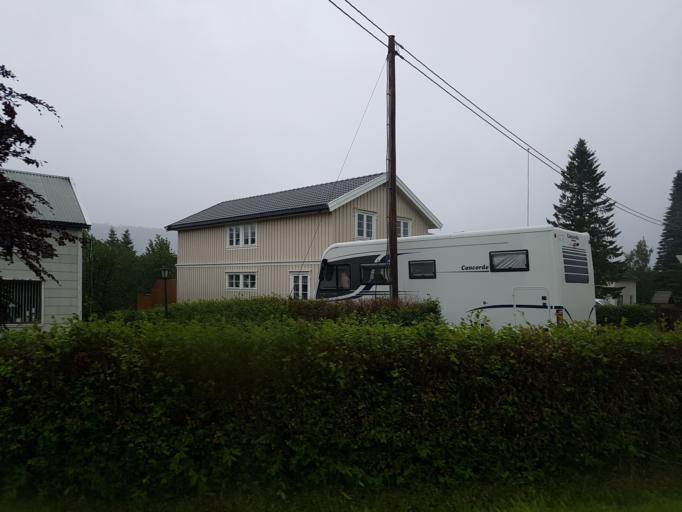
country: NO
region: Nord-Trondelag
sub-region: Stjordal
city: Stjordalshalsen
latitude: 63.4167
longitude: 10.9325
